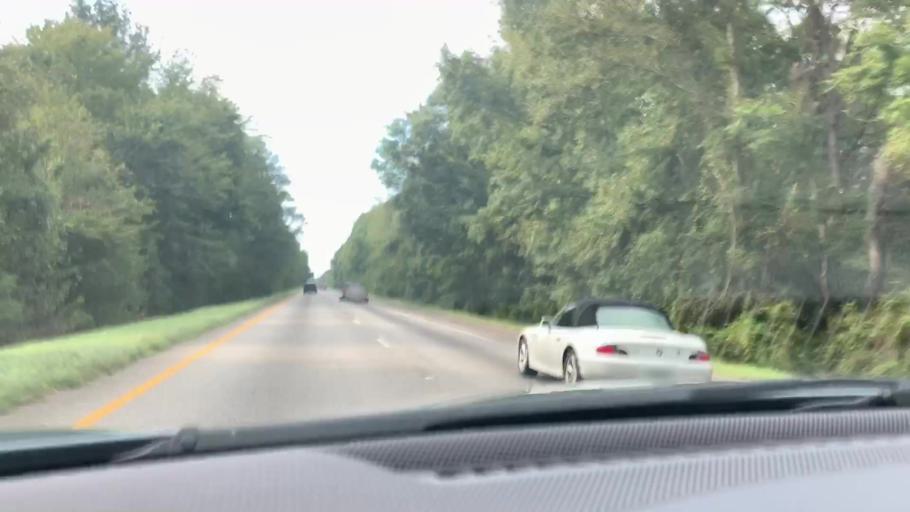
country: US
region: South Carolina
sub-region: Dorchester County
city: Saint George
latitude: 33.3424
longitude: -80.5730
